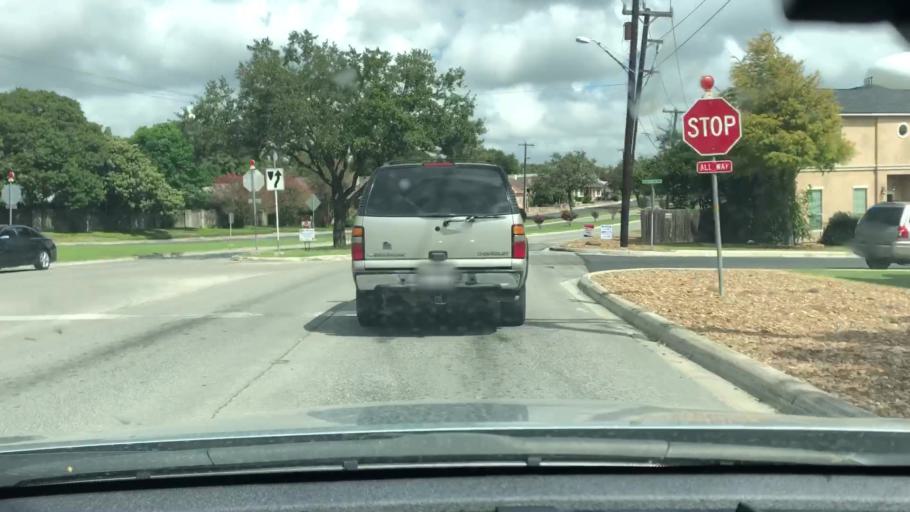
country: US
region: Texas
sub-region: Bexar County
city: Windcrest
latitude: 29.5147
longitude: -98.3715
